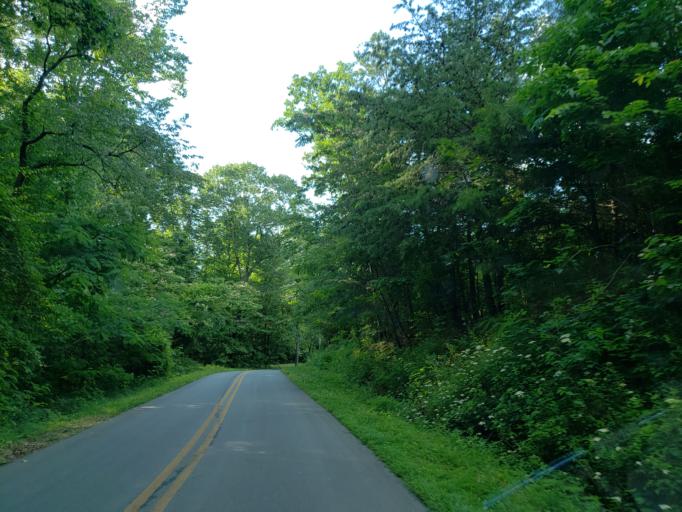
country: US
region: Georgia
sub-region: Haralson County
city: Buchanan
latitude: 33.9025
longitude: -85.2733
